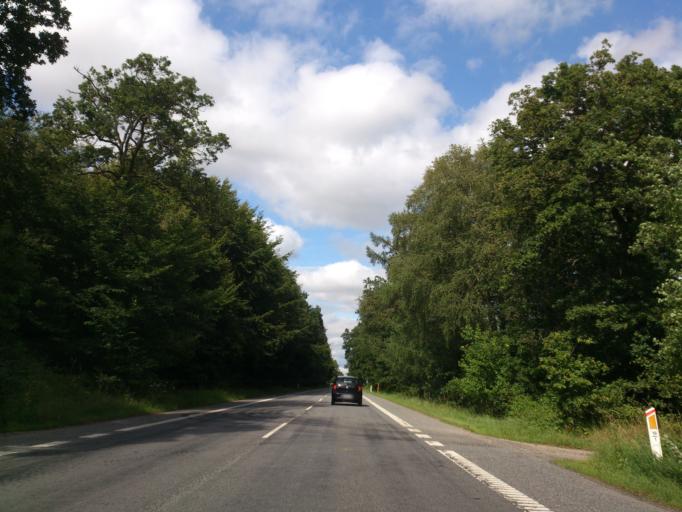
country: DK
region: South Denmark
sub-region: Aabenraa Kommune
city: Krusa
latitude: 54.8815
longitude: 9.4168
